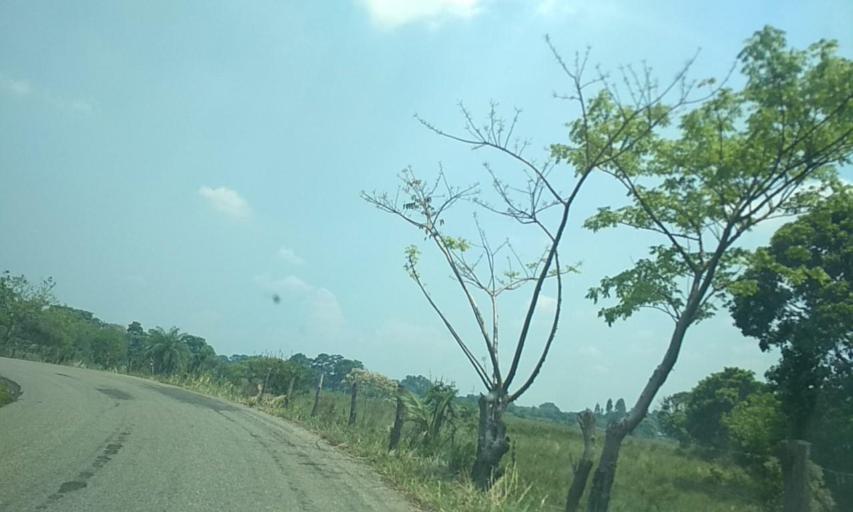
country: MX
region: Tabasco
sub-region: Huimanguillo
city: C-41 (Licenciado Carlos A. Madrazo)
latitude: 17.8488
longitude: -93.5281
